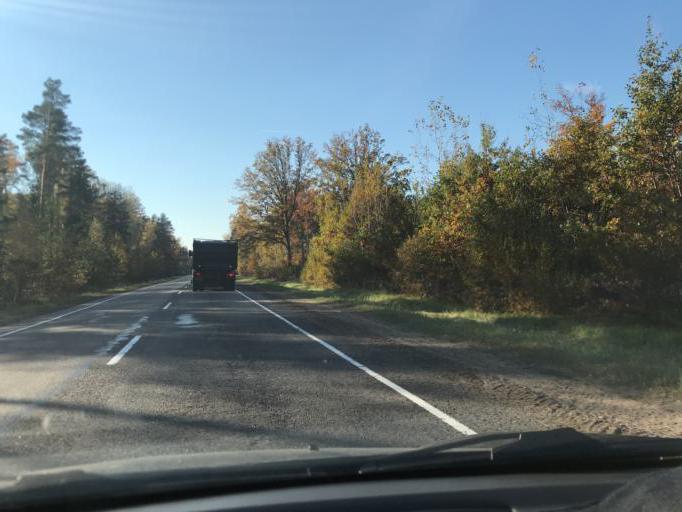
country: BY
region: Mogilev
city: Hlusha
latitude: 53.0901
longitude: 28.8976
